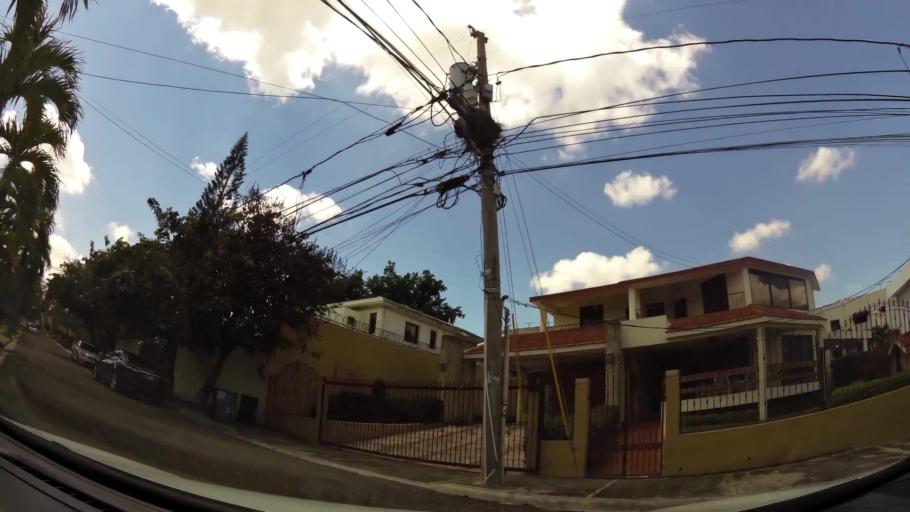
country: DO
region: Santiago
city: Santiago de los Caballeros
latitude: 19.4715
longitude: -70.6761
